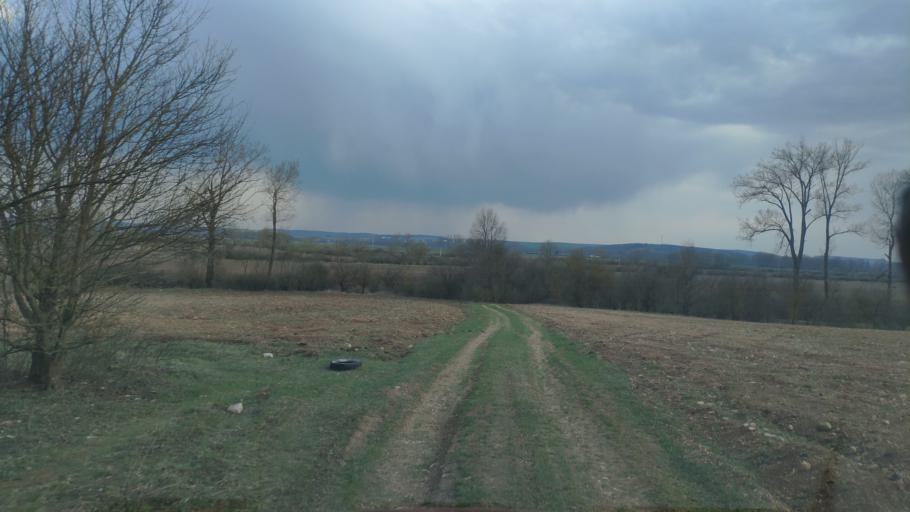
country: SK
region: Kosicky
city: Moldava nad Bodvou
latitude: 48.6167
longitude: 20.9222
